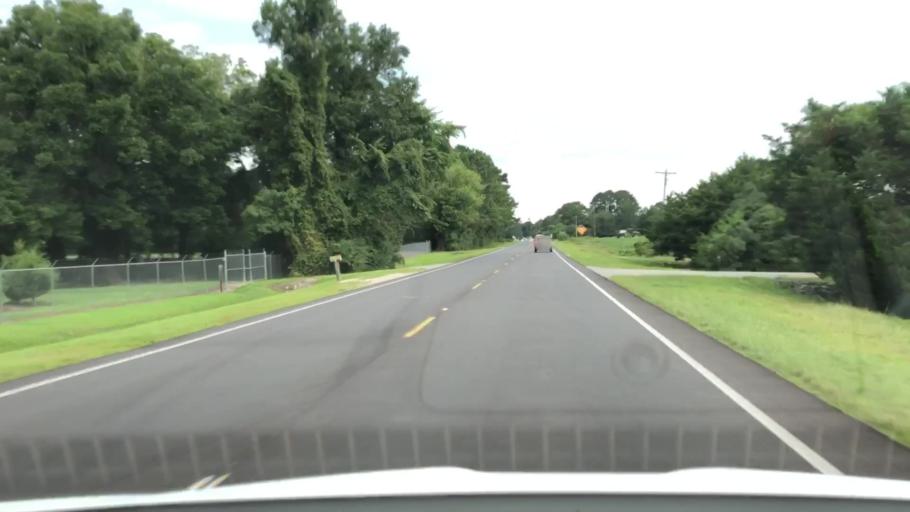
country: US
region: North Carolina
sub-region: Jones County
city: Maysville
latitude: 34.8953
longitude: -77.2187
